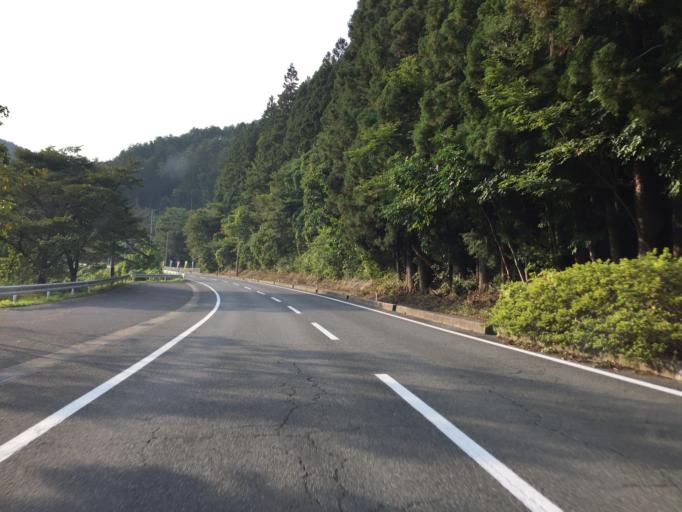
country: JP
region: Fukushima
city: Namie
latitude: 37.5435
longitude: 140.8572
